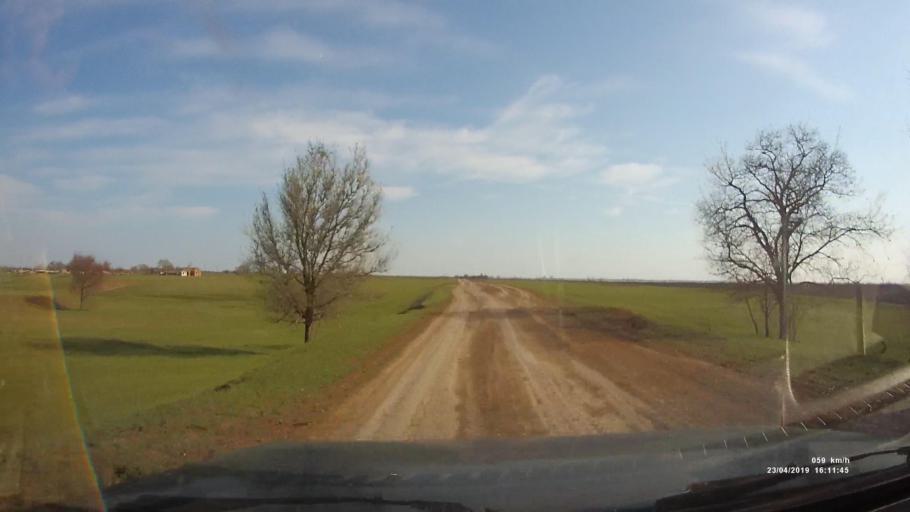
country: RU
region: Rostov
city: Remontnoye
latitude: 46.4730
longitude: 43.1227
